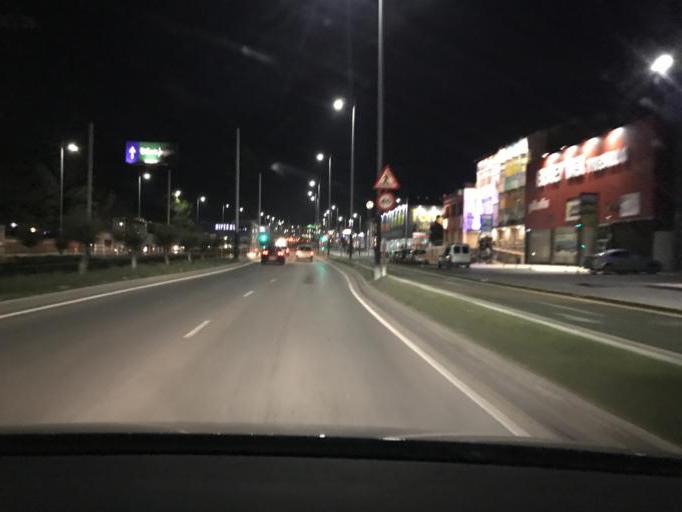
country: ES
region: Andalusia
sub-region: Provincia de Jaen
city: Jaen
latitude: 37.7960
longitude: -3.7796
